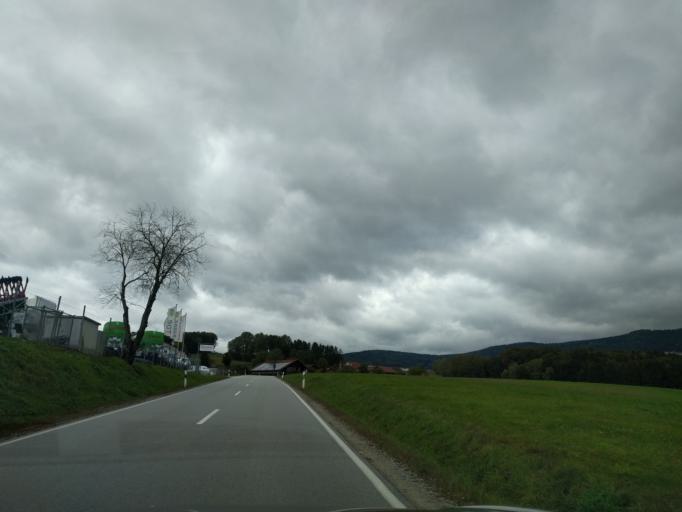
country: DE
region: Bavaria
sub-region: Lower Bavaria
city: Schaufling
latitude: 48.8316
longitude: 13.0831
